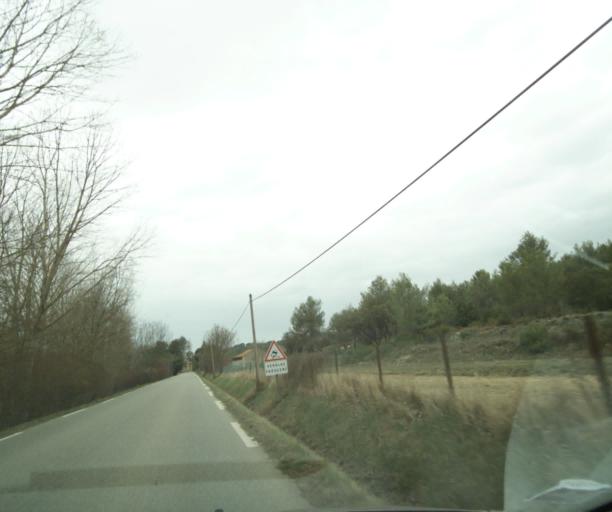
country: FR
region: Provence-Alpes-Cote d'Azur
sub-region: Departement des Bouches-du-Rhone
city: Jouques
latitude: 43.6298
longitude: 5.6589
